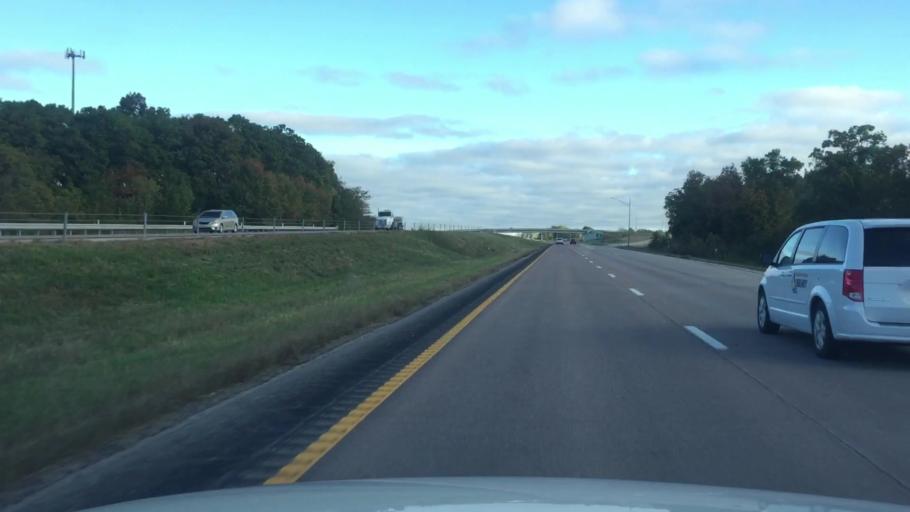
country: US
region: Missouri
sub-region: Boone County
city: Ashland
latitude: 38.8274
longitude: -92.2501
